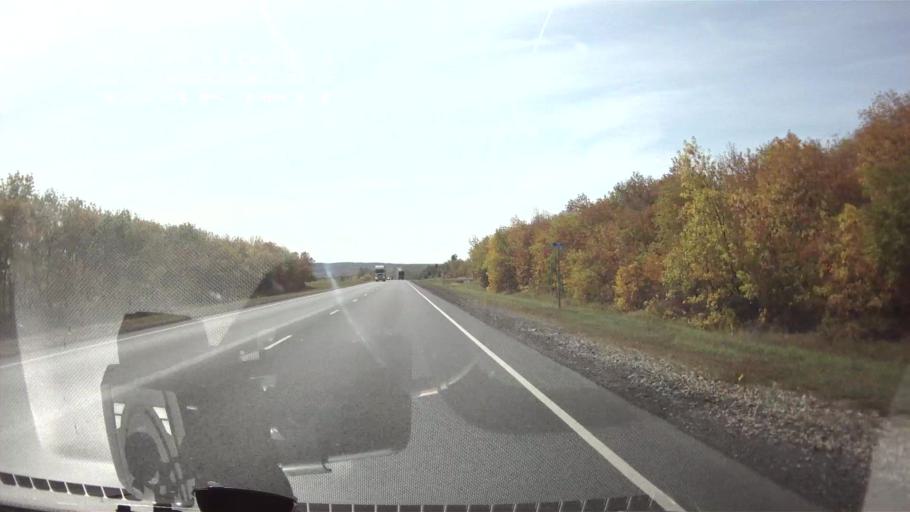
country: RU
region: Saratov
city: Khvalynsk
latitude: 52.5896
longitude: 48.1287
